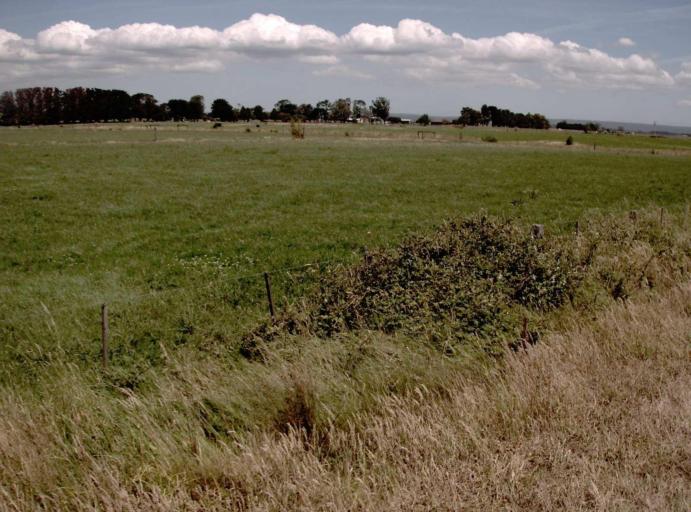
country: AU
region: Victoria
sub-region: Wellington
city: Heyfield
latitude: -38.0684
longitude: 146.8712
